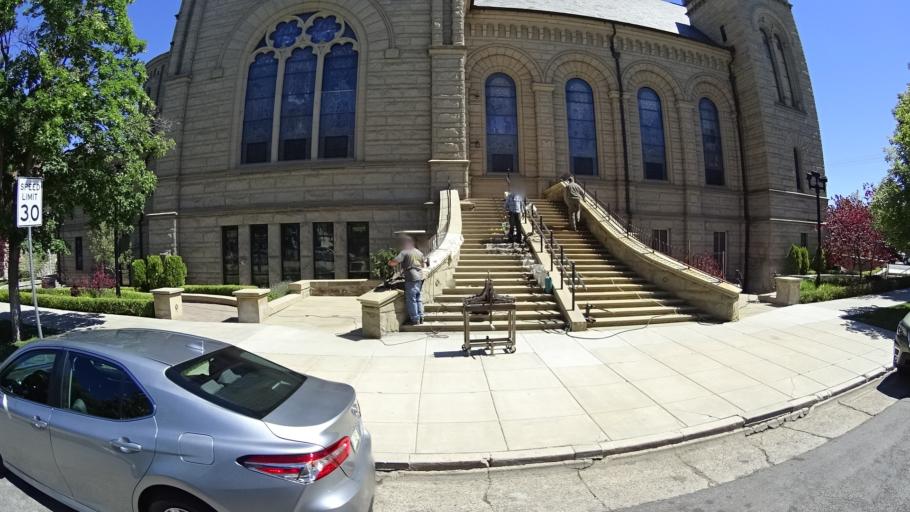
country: US
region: Idaho
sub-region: Ada County
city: Boise
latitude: 43.6212
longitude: -116.1987
